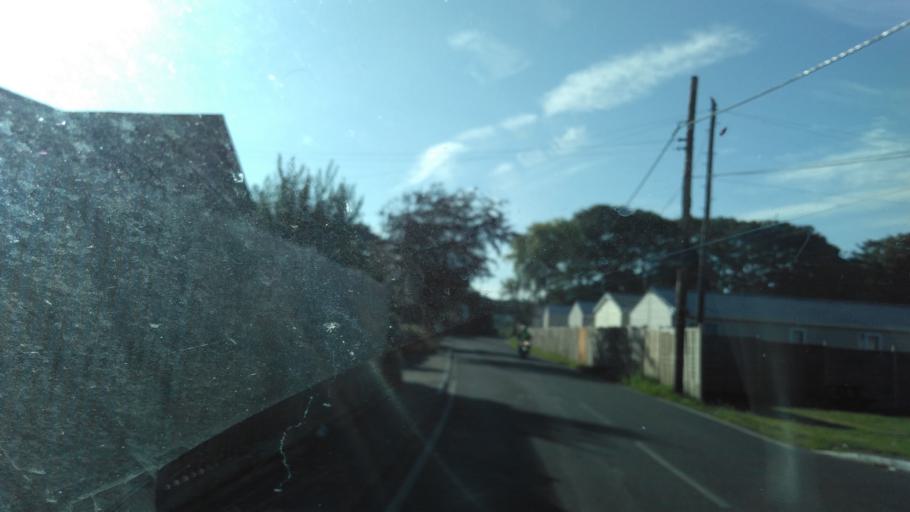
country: GB
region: England
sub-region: Kent
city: Whitstable
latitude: 51.3451
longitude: 0.9901
